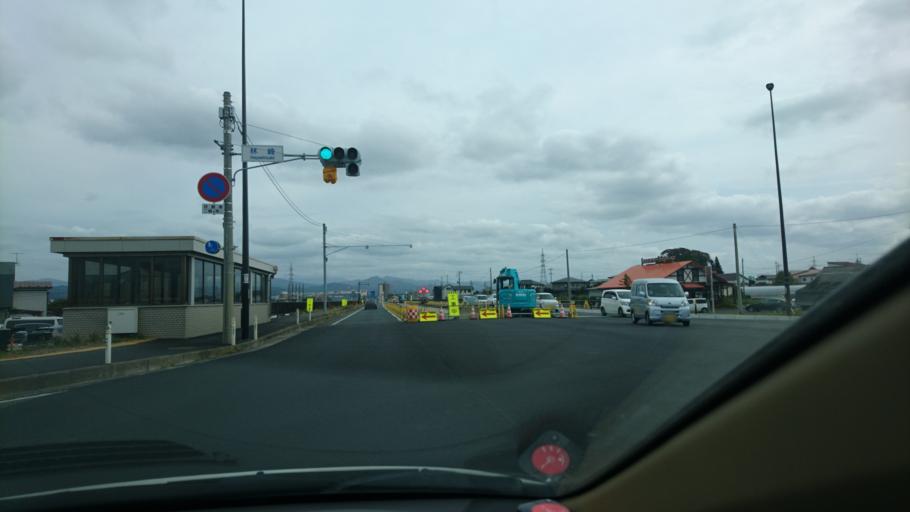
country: JP
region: Iwate
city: Morioka-shi
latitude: 39.6900
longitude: 141.1116
